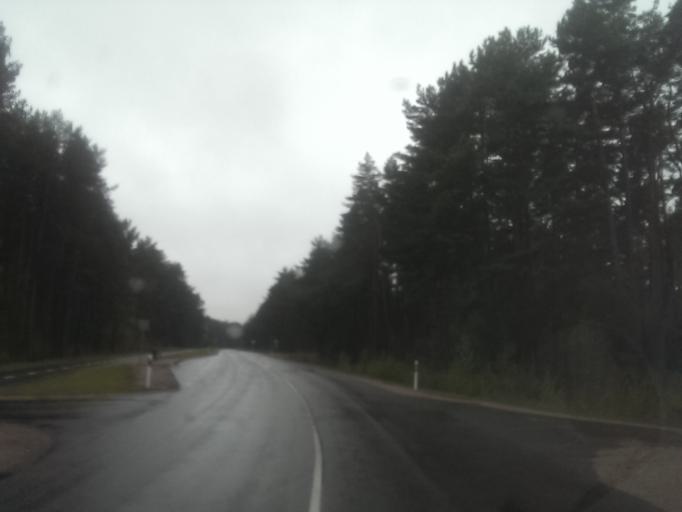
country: LV
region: Ventspils
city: Ventspils
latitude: 57.4184
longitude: 21.6277
